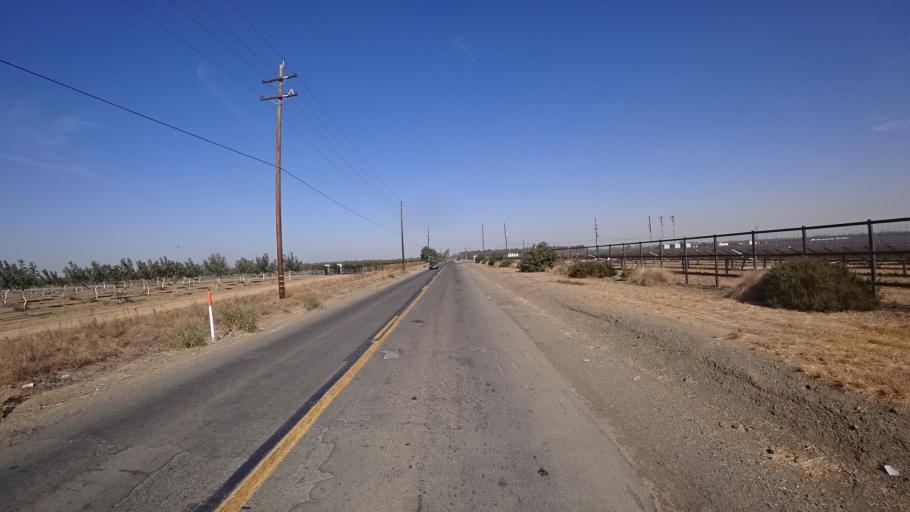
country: US
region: California
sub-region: Yolo County
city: Davis
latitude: 38.5007
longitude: -121.6955
